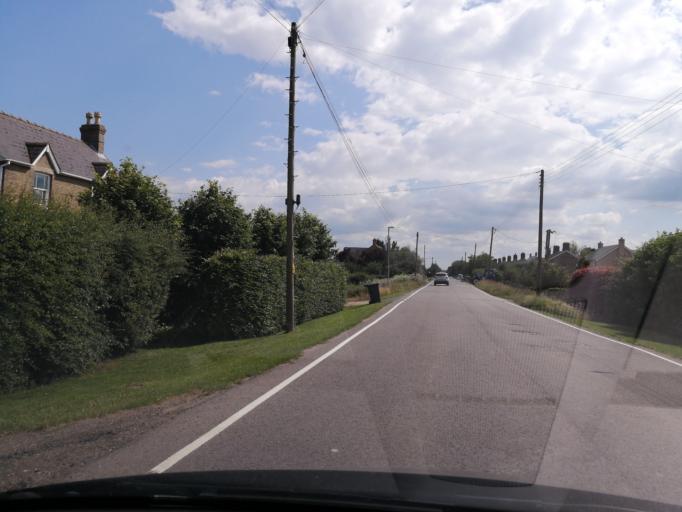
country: GB
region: England
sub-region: Cambridgeshire
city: Ramsey
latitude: 52.4572
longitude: -0.1567
